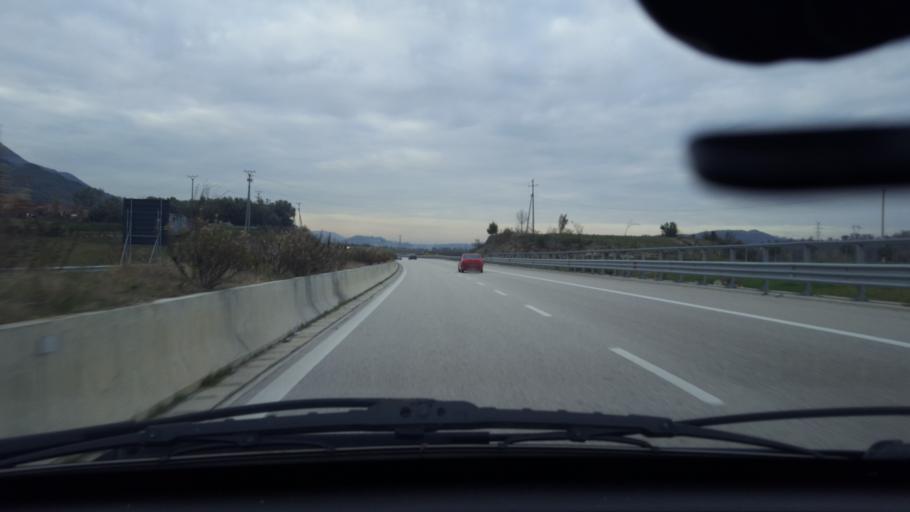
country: AL
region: Tirane
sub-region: Rrethi i Tiranes
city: Berzhite
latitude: 41.2458
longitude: 19.9100
